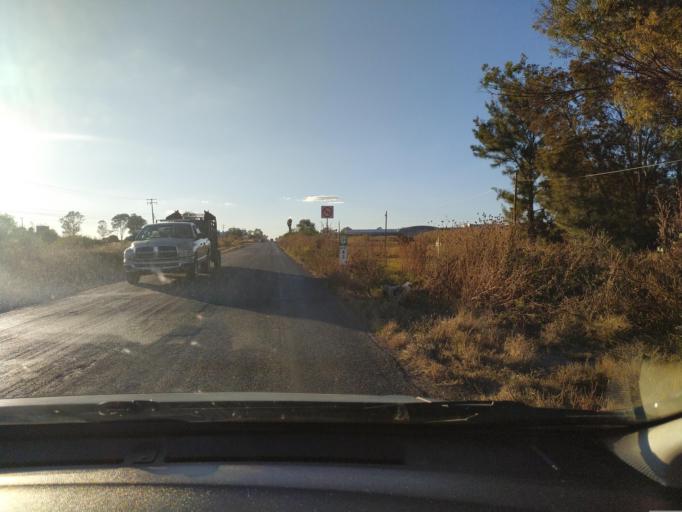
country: MX
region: Jalisco
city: San Julian
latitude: 21.0077
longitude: -102.1526
